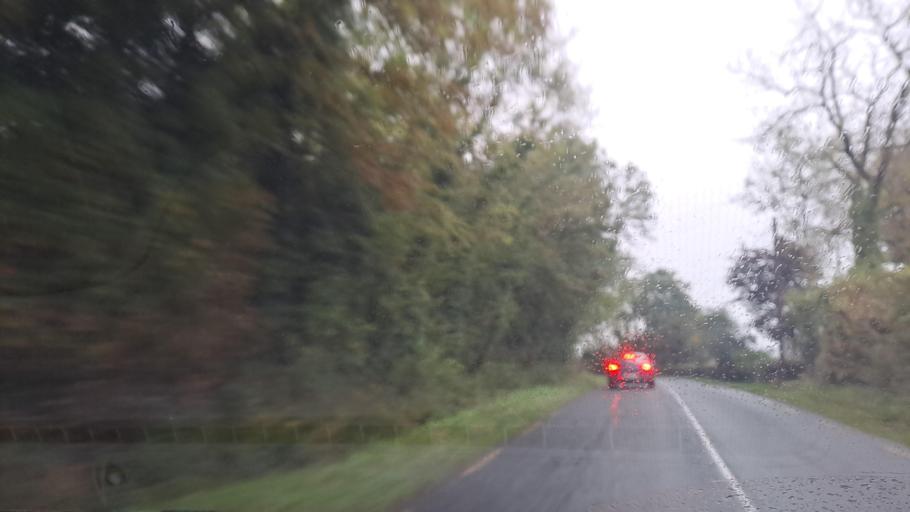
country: IE
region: Ulster
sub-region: County Monaghan
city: Monaghan
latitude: 54.2233
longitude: -6.9308
